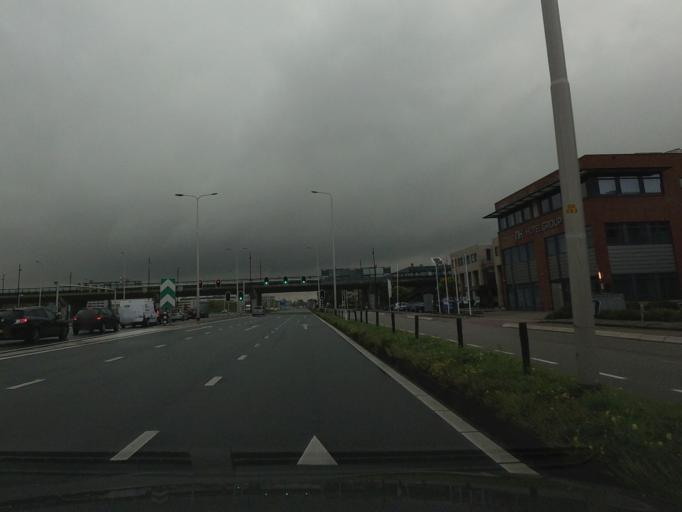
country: NL
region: North Holland
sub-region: Gemeente Haarlemmermeer
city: Hoofddorp
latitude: 52.2899
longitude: 4.7218
